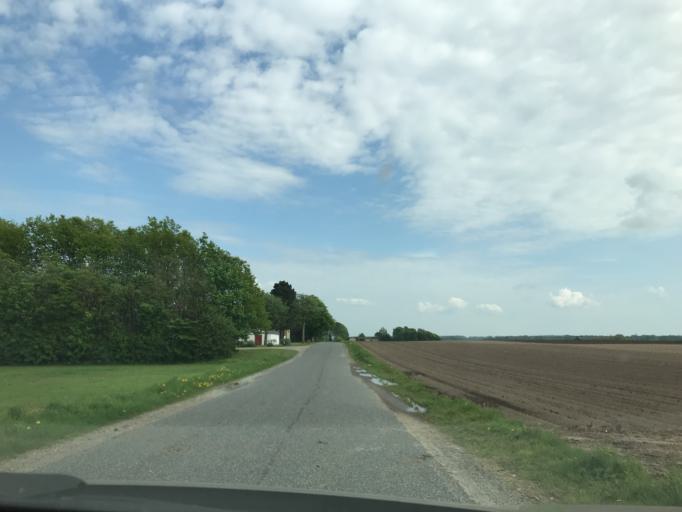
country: DK
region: South Denmark
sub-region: Assens Kommune
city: Assens
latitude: 55.3282
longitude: 9.9024
